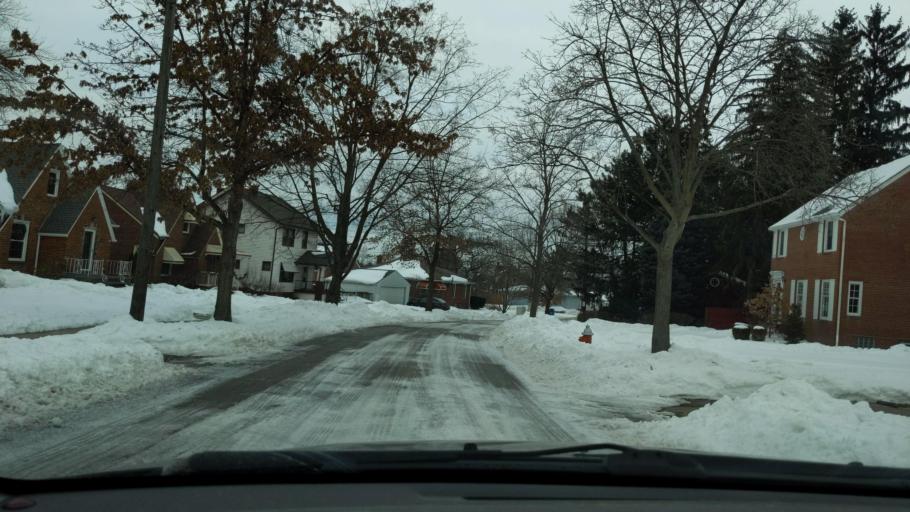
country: US
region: Ohio
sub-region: Cuyahoga County
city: Brooklyn Heights
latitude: 41.4253
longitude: -81.6898
